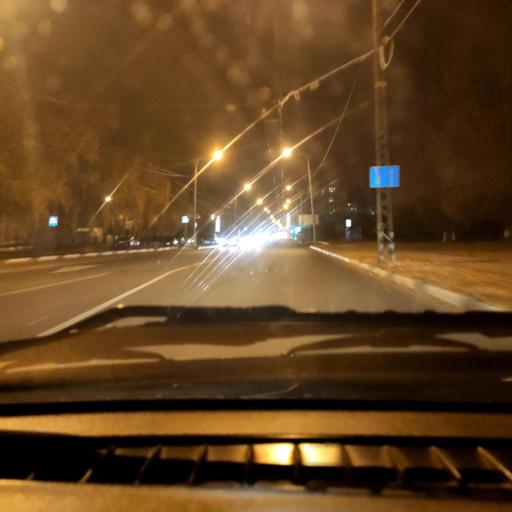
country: RU
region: Samara
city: Tol'yatti
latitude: 53.4996
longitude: 49.4106
